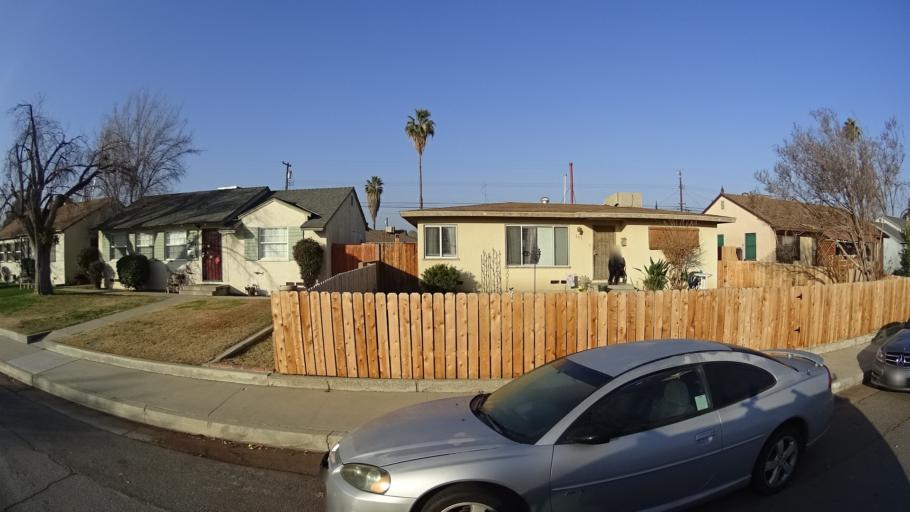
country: US
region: California
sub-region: Kern County
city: Bakersfield
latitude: 35.3592
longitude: -119.0405
